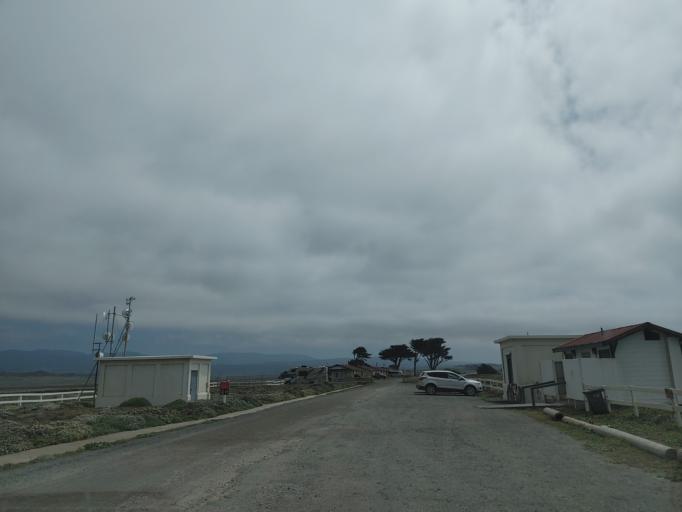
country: US
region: California
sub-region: Sonoma County
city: Sea Ranch
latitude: 38.9546
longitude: -123.7407
